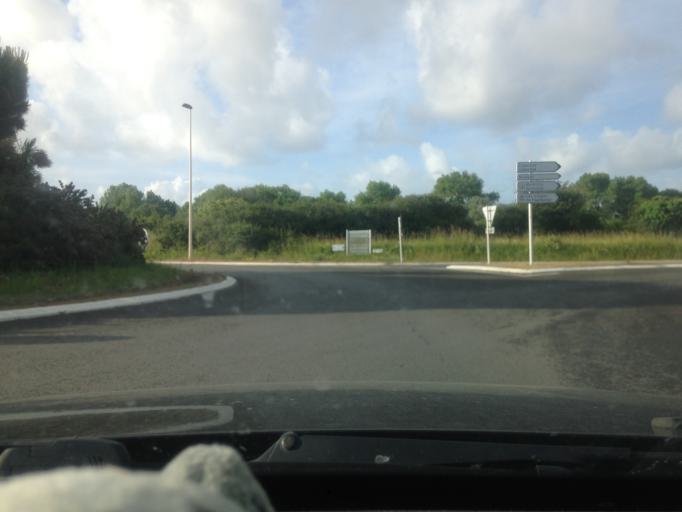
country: FR
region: Brittany
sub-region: Departement du Morbihan
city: Erdeven
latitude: 47.6207
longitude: -3.1355
